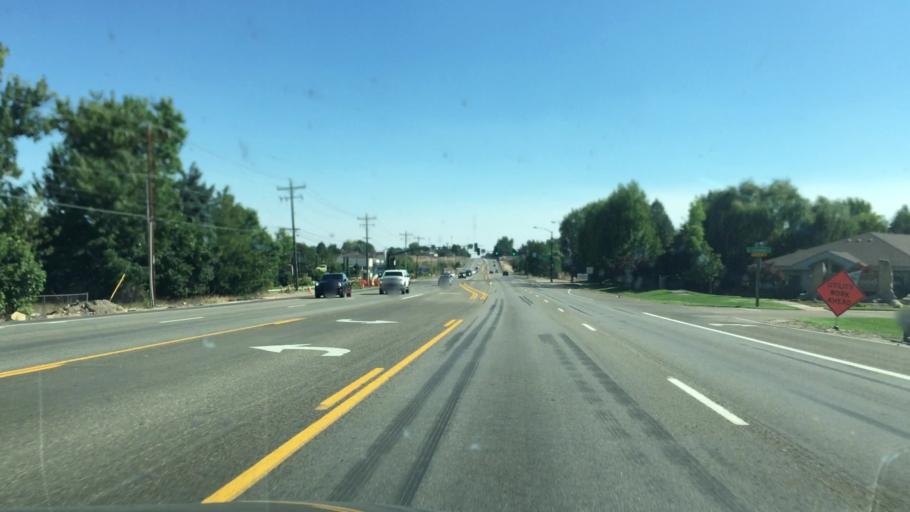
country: US
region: Idaho
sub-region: Ada County
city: Eagle
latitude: 43.6737
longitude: -116.3543
